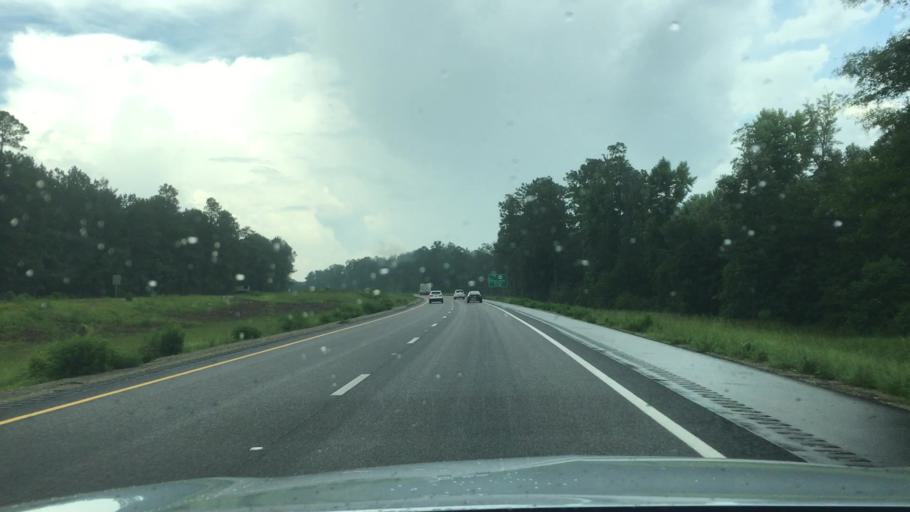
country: US
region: Mississippi
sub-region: Lamar County
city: West Hattiesburg
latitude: 31.2249
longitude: -89.3242
